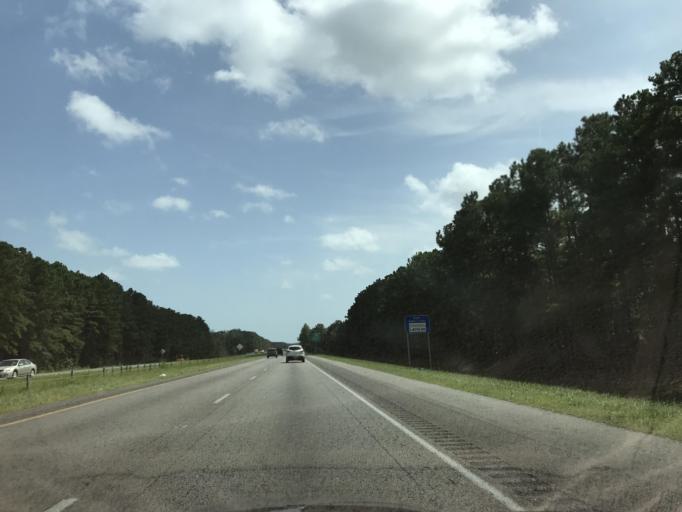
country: US
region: North Carolina
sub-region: New Hanover County
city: Skippers Corner
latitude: 34.3430
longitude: -77.8804
